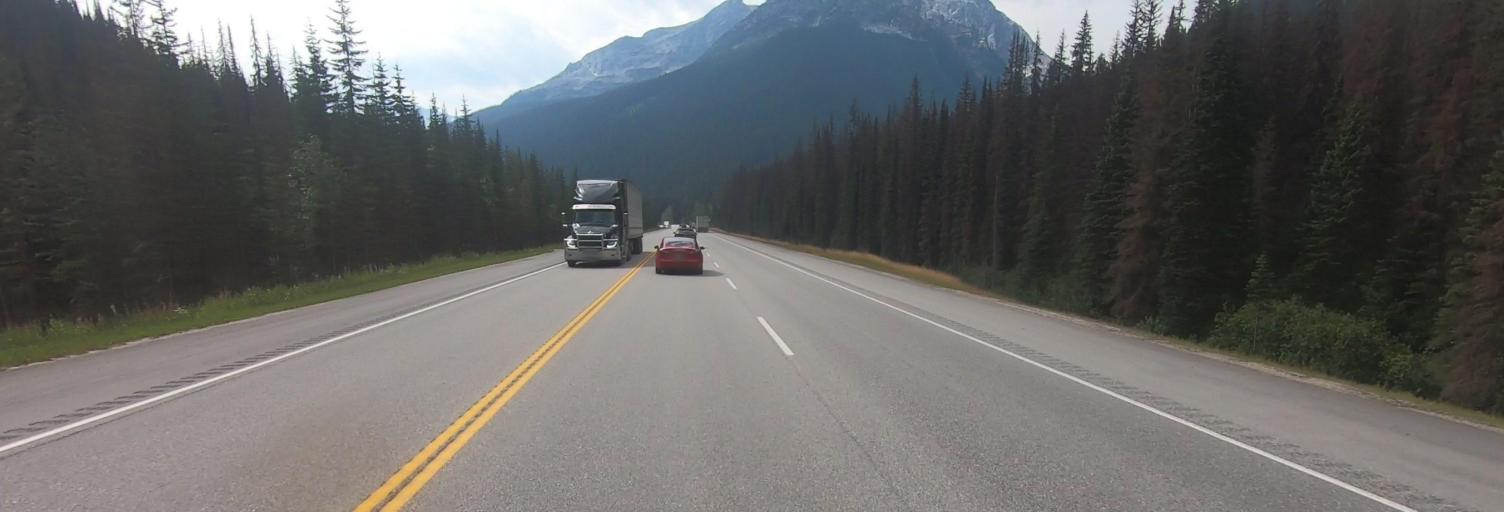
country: CA
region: British Columbia
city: Golden
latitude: 51.3108
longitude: -117.5160
